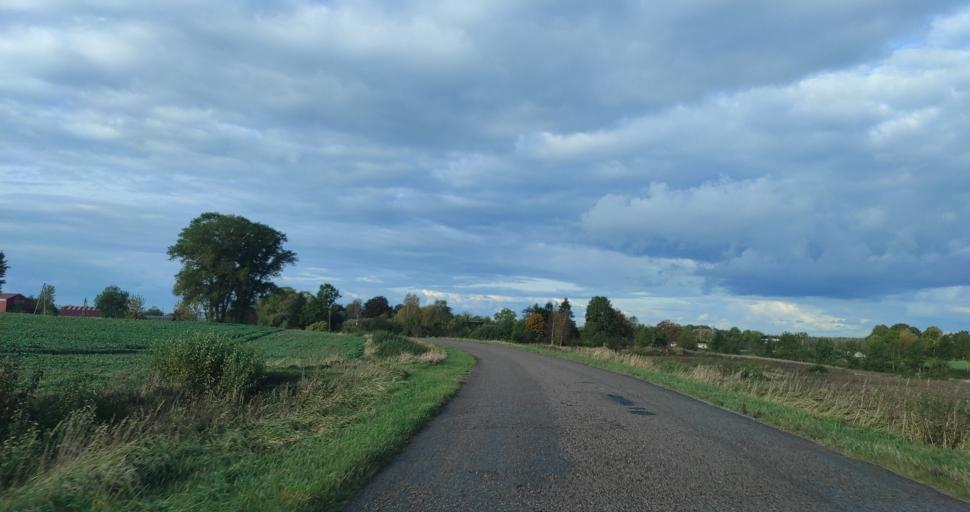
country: LV
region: Aizpute
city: Aizpute
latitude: 56.7836
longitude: 21.7637
